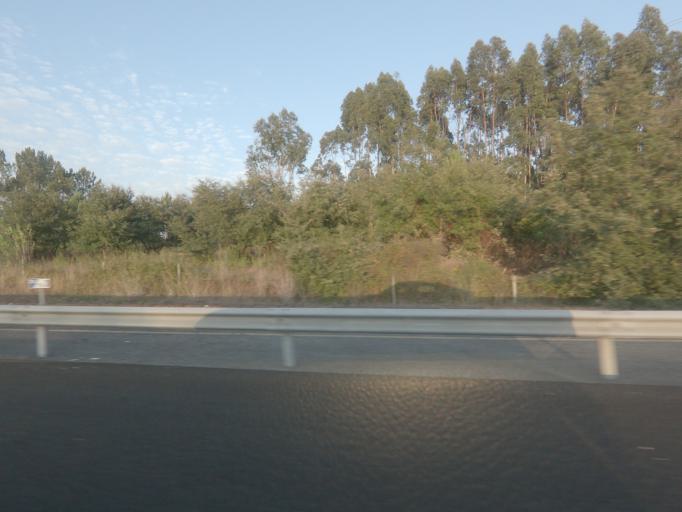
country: PT
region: Leiria
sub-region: Leiria
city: Caranguejeira
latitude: 39.7705
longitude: -8.7442
